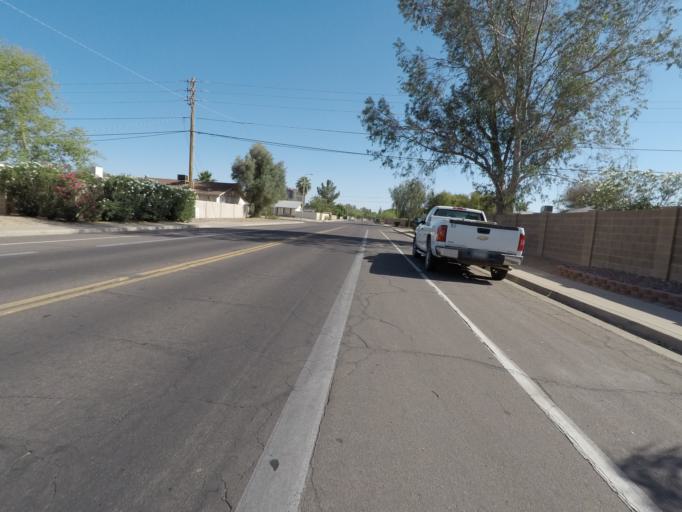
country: US
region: Arizona
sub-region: Maricopa County
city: Tempe
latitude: 33.3989
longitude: -111.9163
